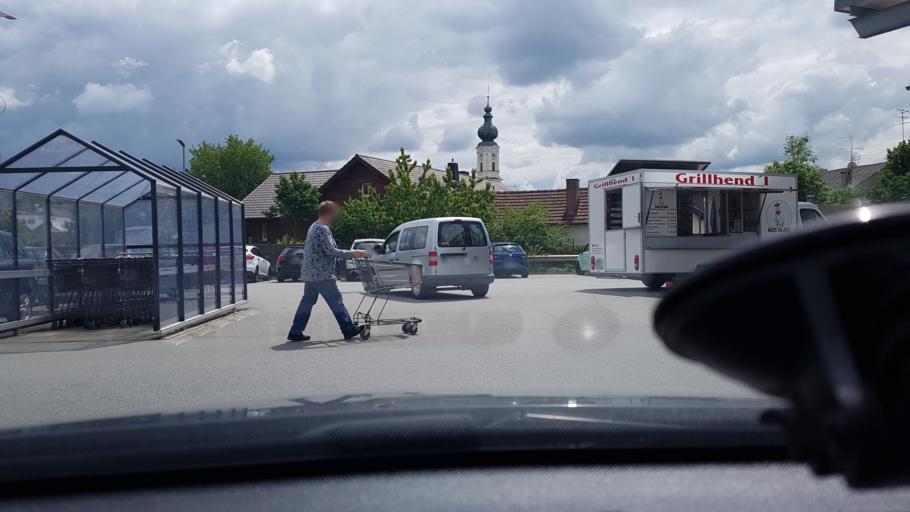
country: DE
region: Bavaria
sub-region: Lower Bavaria
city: Rotthalmunster
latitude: 48.3611
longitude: 13.2007
